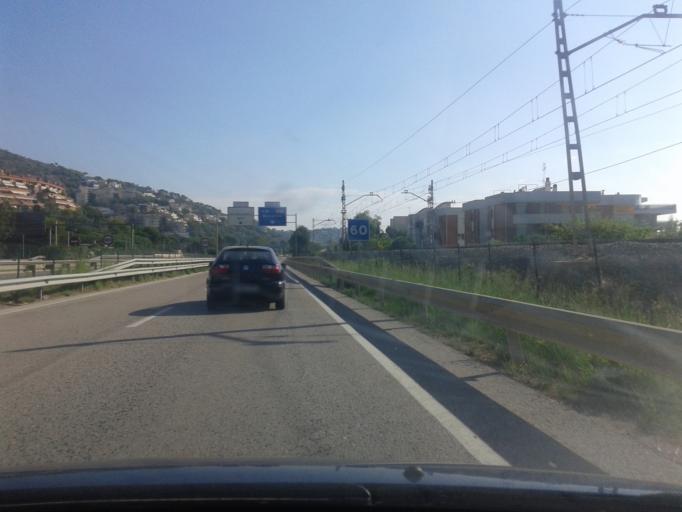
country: ES
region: Catalonia
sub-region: Provincia de Barcelona
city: Castelldefels
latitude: 41.2635
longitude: 1.9318
